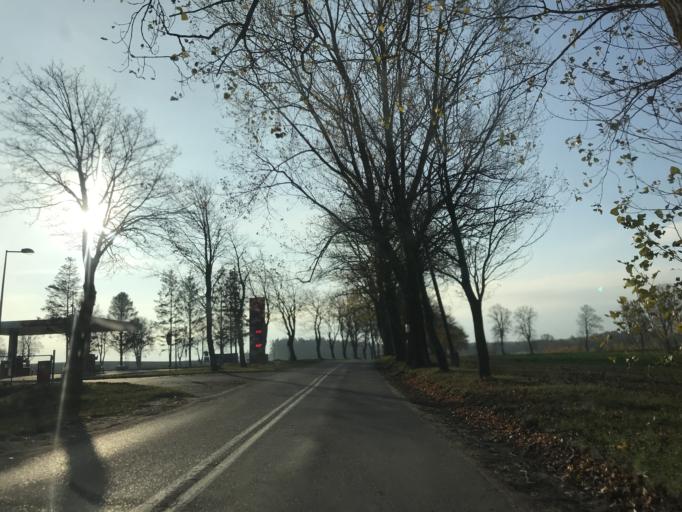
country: PL
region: Pomeranian Voivodeship
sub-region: Powiat pucki
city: Krokowa
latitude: 54.7883
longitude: 18.1180
